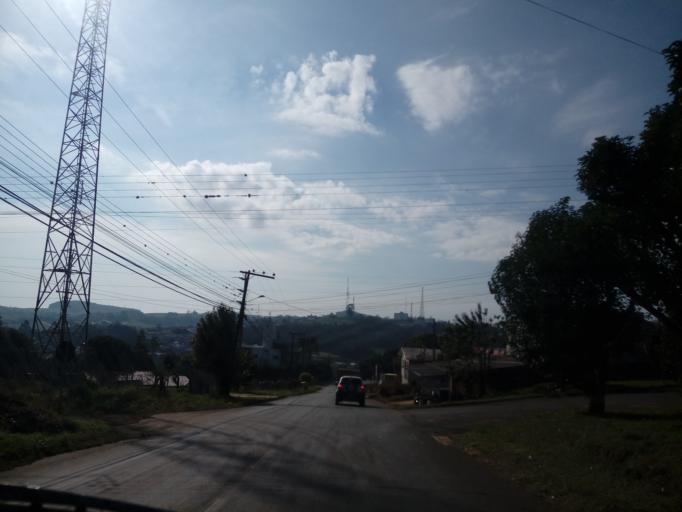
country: BR
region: Santa Catarina
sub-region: Chapeco
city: Chapeco
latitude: -27.1088
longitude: -52.5953
